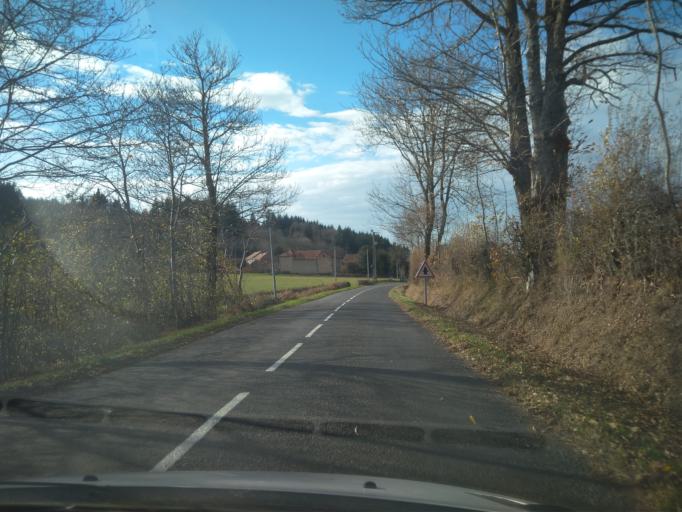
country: FR
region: Auvergne
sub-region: Departement de l'Allier
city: Le Mayet-de-Montagne
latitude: 46.1394
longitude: 3.7546
